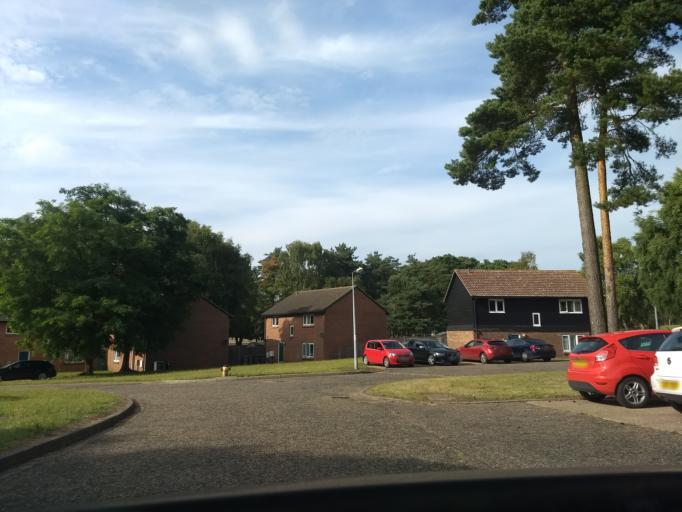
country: GB
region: England
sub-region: Suffolk
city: Woodbridge
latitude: 52.0816
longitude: 1.3901
